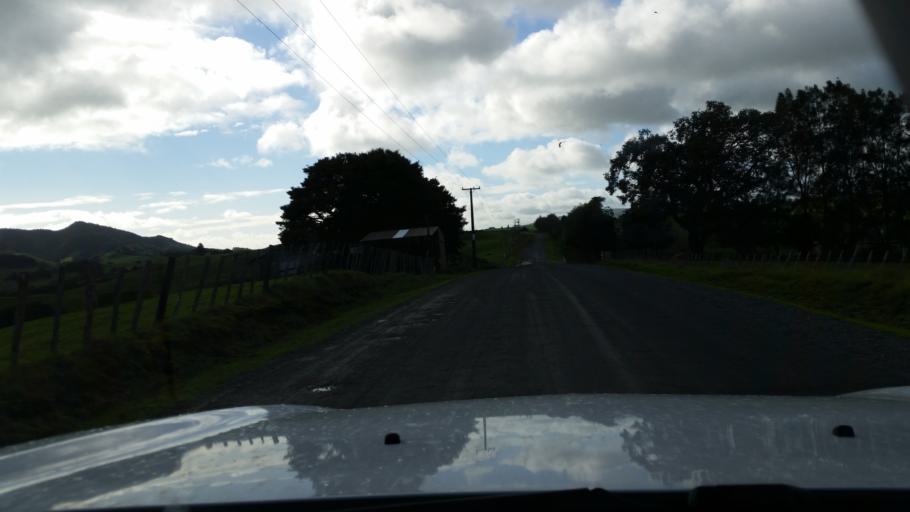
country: NZ
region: Northland
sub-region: Whangarei
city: Maungatapere
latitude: -35.6647
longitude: 174.1045
